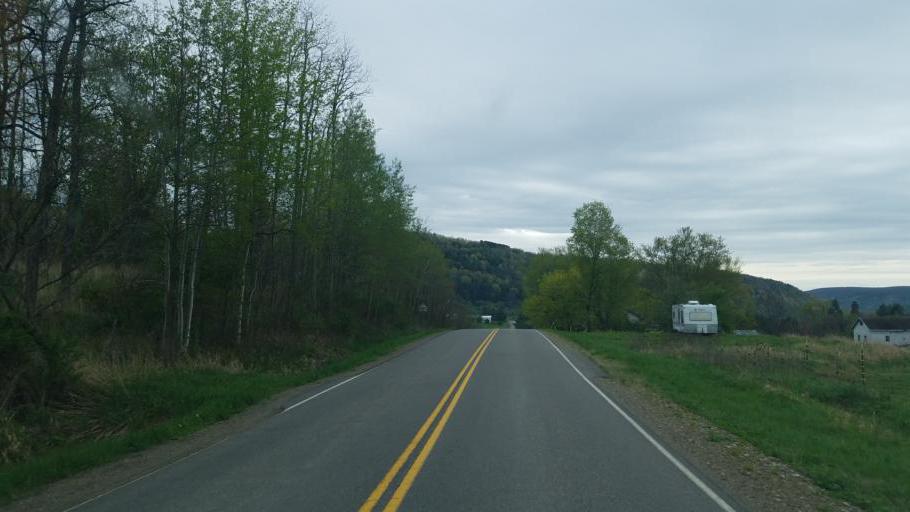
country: US
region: Pennsylvania
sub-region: Tioga County
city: Westfield
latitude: 42.0265
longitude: -77.4663
